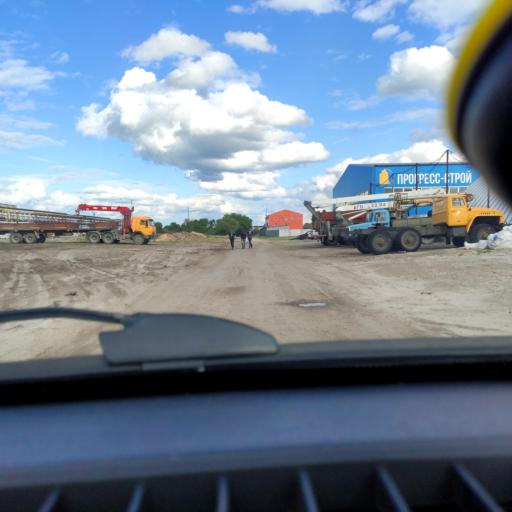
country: RU
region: Samara
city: Tol'yatti
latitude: 53.5458
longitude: 49.4770
